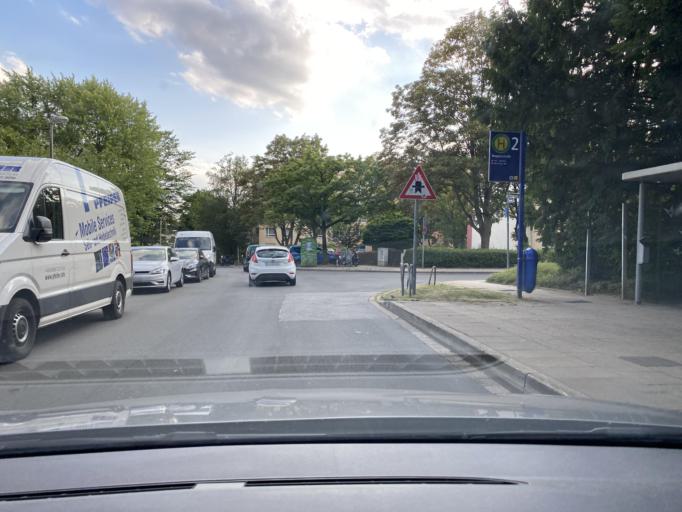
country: DE
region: North Rhine-Westphalia
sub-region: Regierungsbezirk Dusseldorf
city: Heiligenhaus
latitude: 51.3743
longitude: 6.9387
